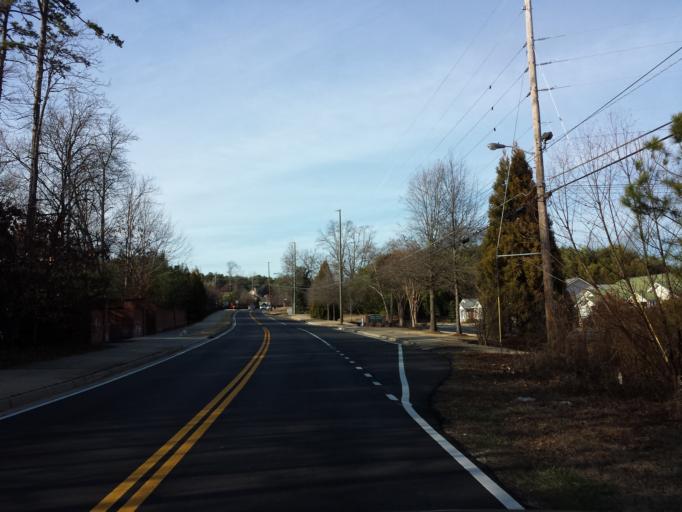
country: US
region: Georgia
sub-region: Cobb County
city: Marietta
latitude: 33.9753
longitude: -84.5665
